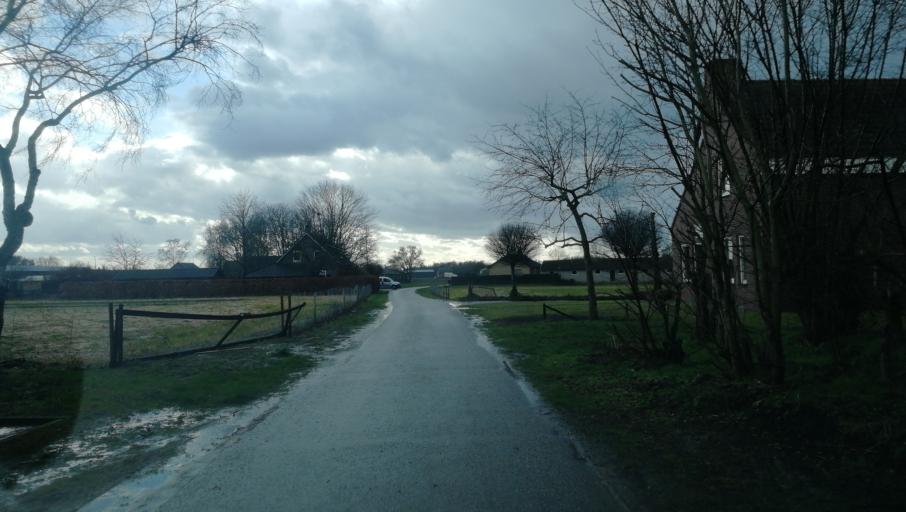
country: NL
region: Limburg
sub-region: Gemeente Peel en Maas
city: Maasbree
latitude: 51.3507
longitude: 6.0535
